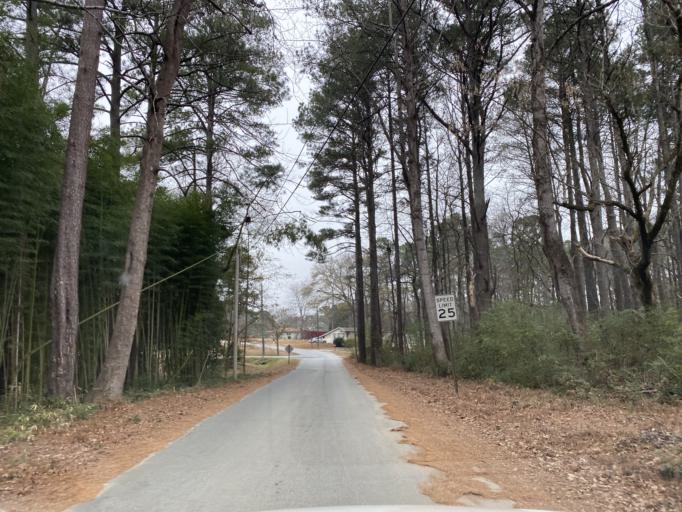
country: US
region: Georgia
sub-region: Cobb County
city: Fair Oaks
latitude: 33.9079
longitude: -84.5713
